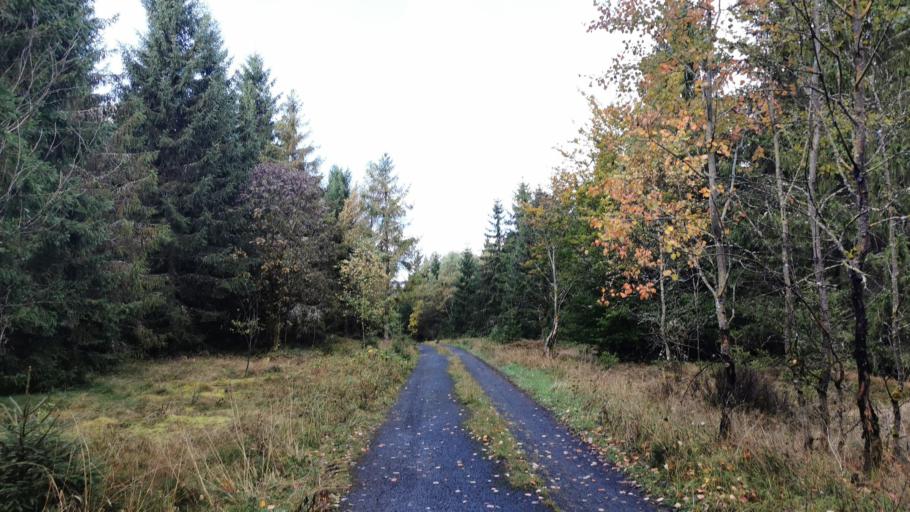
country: DE
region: Bavaria
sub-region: Upper Franconia
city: Tettau
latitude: 50.4890
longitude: 11.2919
